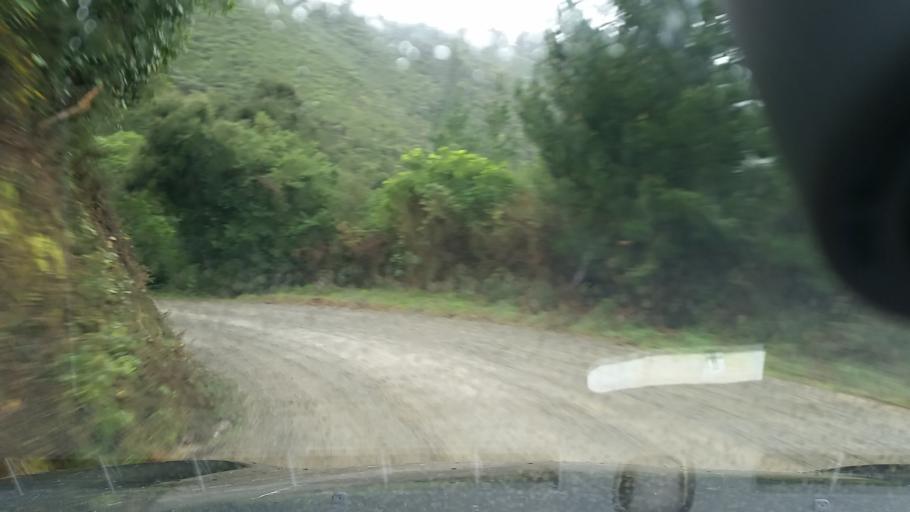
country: NZ
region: Marlborough
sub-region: Marlborough District
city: Picton
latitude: -41.3469
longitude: 174.0746
